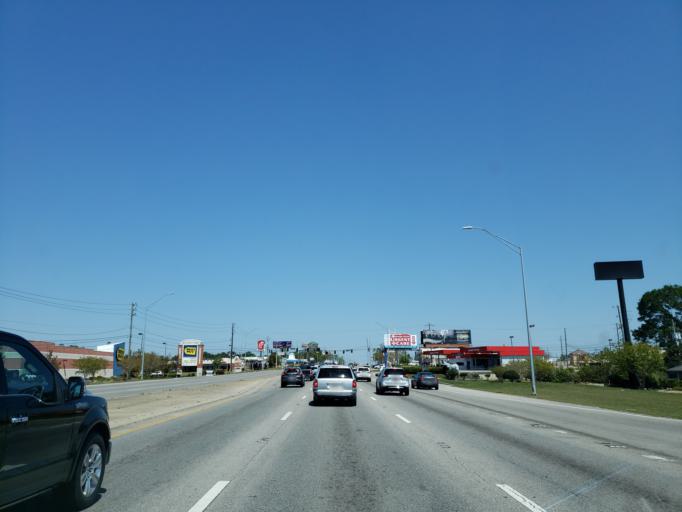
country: US
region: Mississippi
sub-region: Harrison County
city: West Gulfport
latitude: 30.4402
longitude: -89.0977
